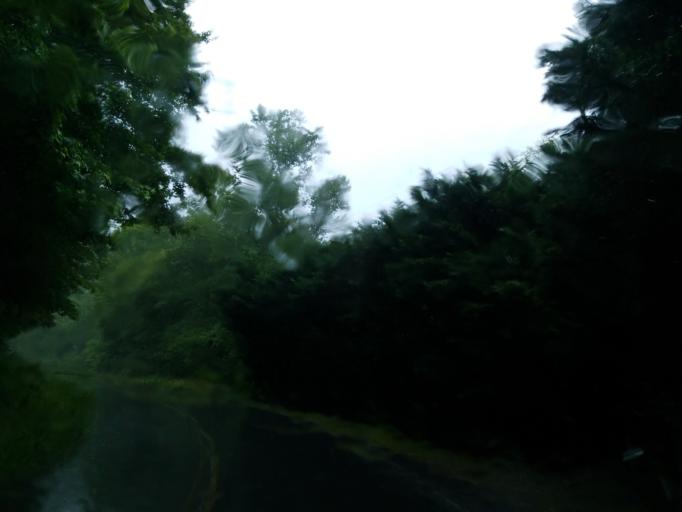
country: US
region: Georgia
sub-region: Fannin County
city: Blue Ridge
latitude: 34.7818
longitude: -84.2868
